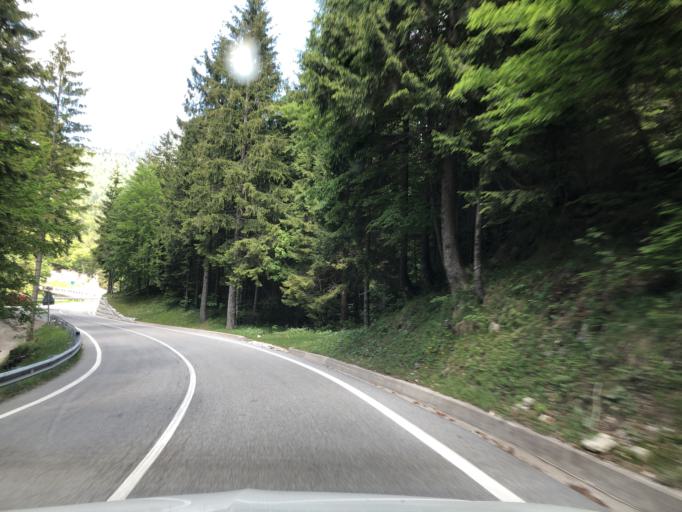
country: IT
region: Friuli Venezia Giulia
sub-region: Provincia di Udine
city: Tarvisio
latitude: 46.4263
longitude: 13.5697
